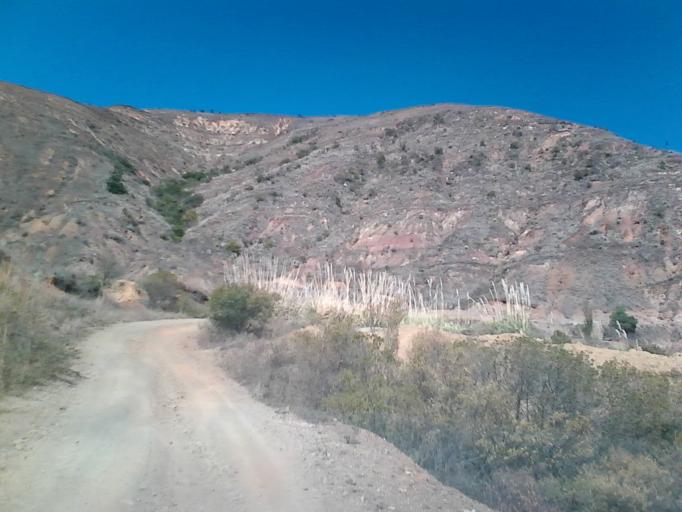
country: CO
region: Boyaca
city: Sachica
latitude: 5.5650
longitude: -73.5565
